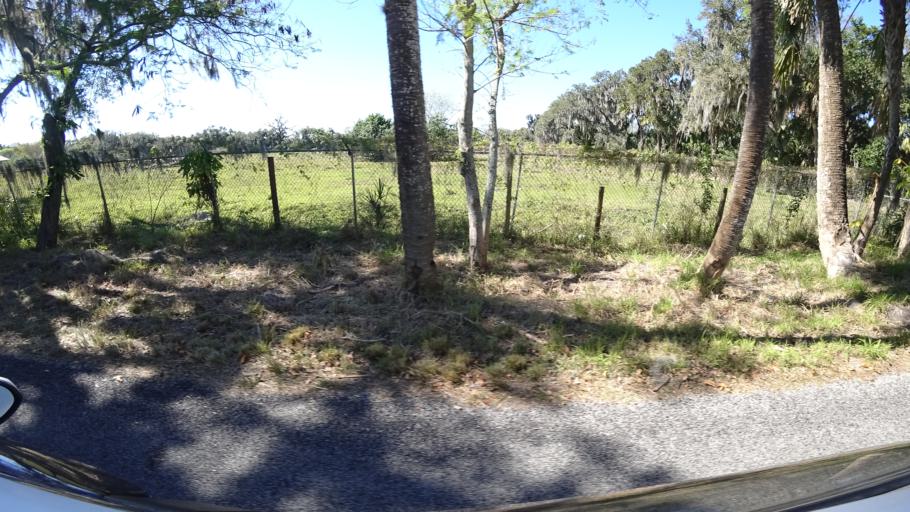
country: US
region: Florida
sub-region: Manatee County
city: Memphis
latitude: 27.5453
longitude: -82.5401
